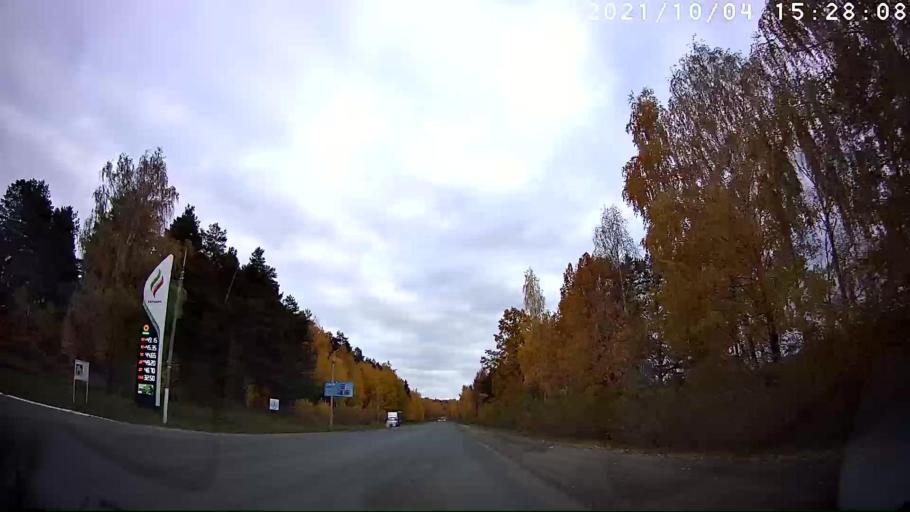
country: RU
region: Mariy-El
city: Yoshkar-Ola
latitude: 56.6127
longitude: 47.9617
